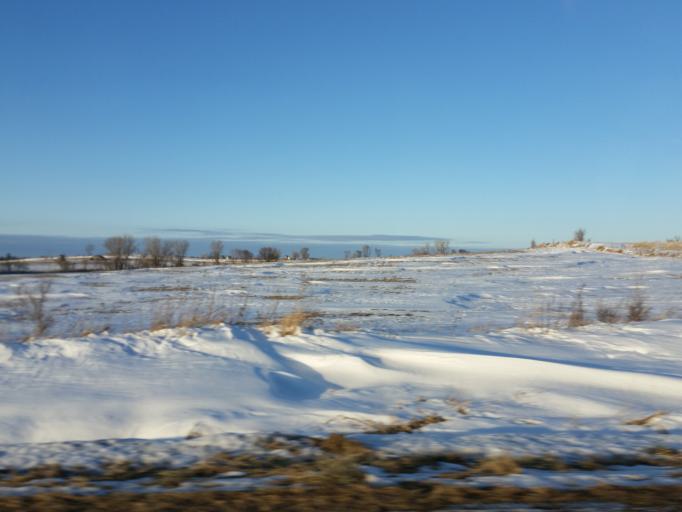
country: US
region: Iowa
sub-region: Butler County
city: Allison
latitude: 42.7449
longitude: -92.8967
